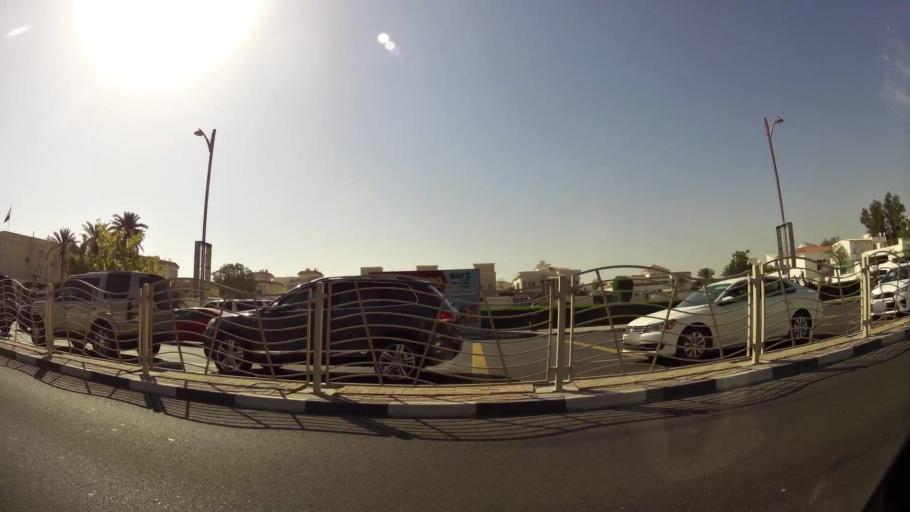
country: AE
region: Dubai
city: Dubai
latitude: 25.1421
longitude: 55.1925
